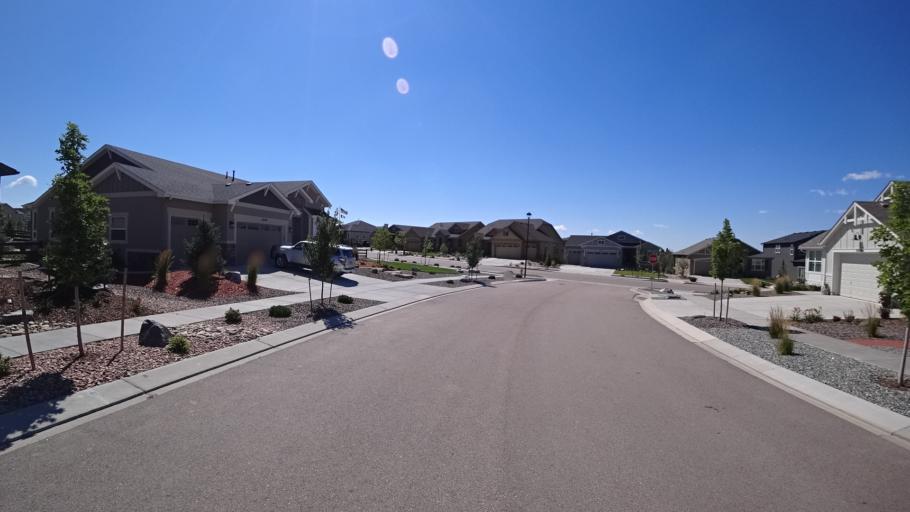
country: US
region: Colorado
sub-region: El Paso County
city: Black Forest
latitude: 38.9816
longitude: -104.7516
